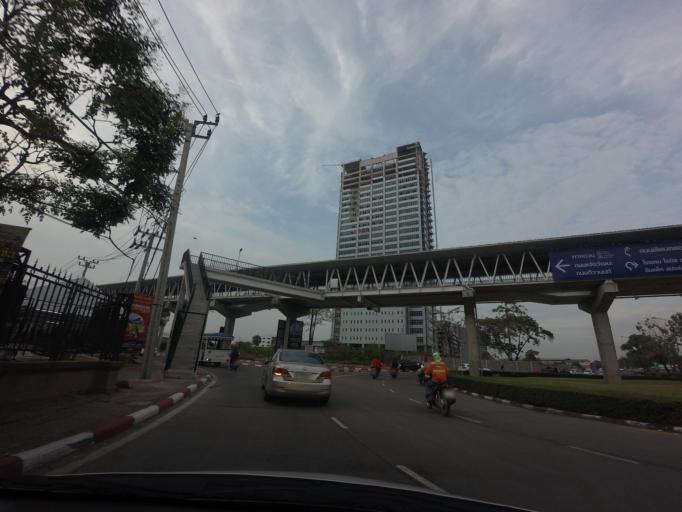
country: TH
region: Bangkok
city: Don Mueang
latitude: 13.9158
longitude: 100.5511
